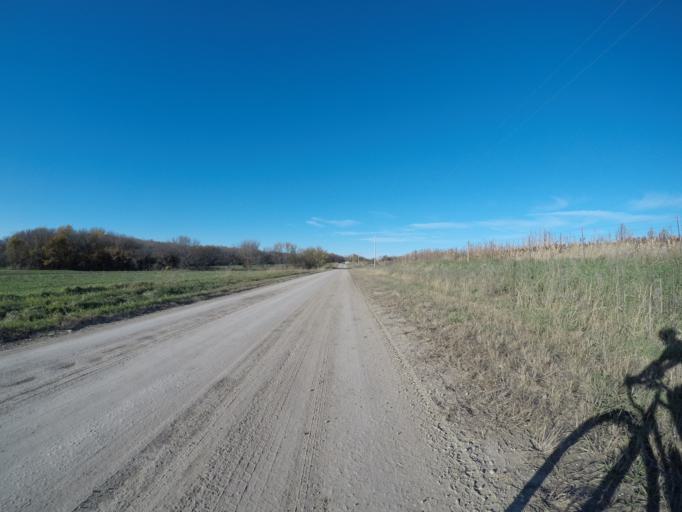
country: US
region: Kansas
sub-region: Riley County
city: Fort Riley North
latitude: 39.2723
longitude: -96.7844
